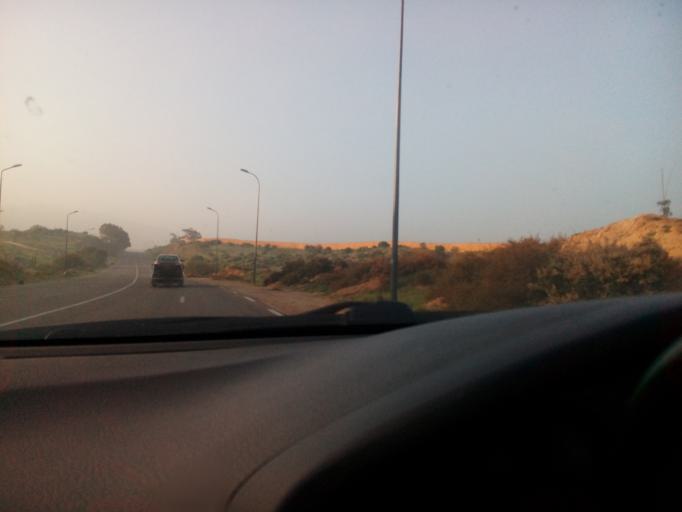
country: DZ
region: Oran
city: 'Ain el Turk
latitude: 35.7202
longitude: -0.8516
